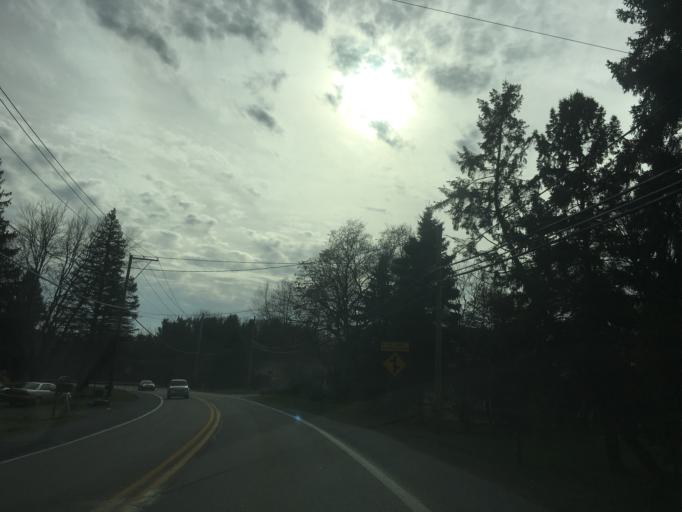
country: US
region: Pennsylvania
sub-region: Dauphin County
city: Colonial Park
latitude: 40.3245
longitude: -76.8266
